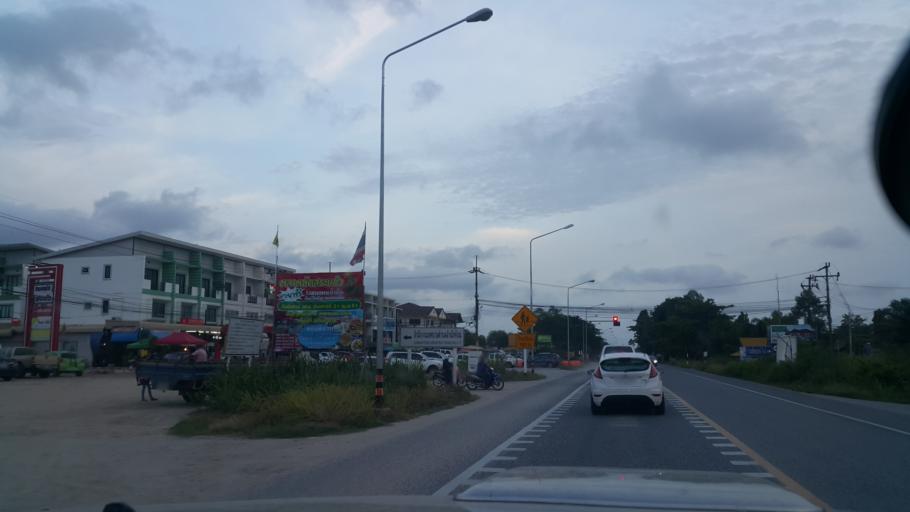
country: TH
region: Rayong
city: Ban Chang
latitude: 12.7141
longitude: 101.0006
